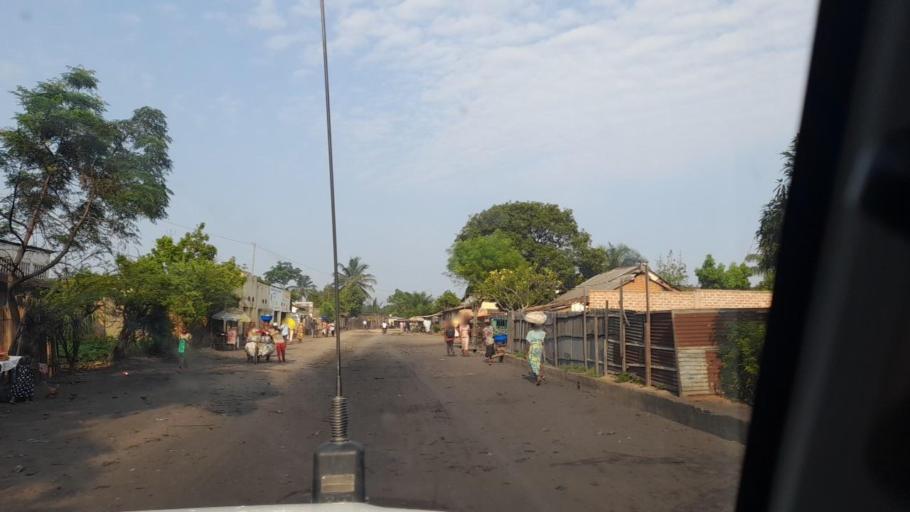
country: CD
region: Kasai-Occidental
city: Kananga
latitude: -5.8950
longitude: 22.3903
